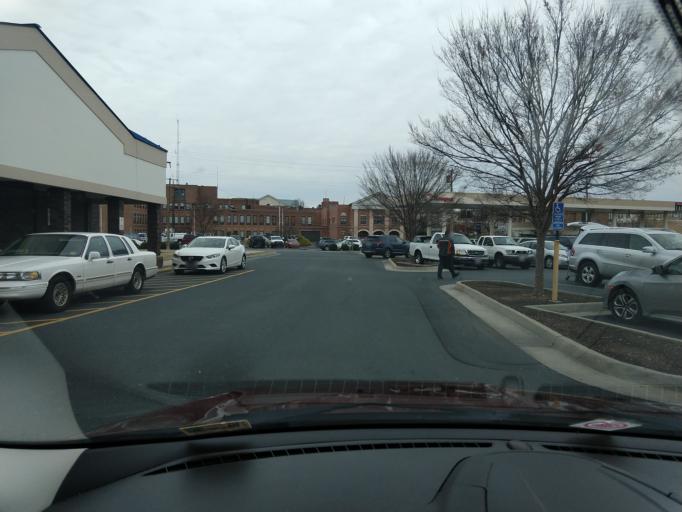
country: US
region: Virginia
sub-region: City of Waynesboro
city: Waynesboro
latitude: 38.0660
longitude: -78.8883
